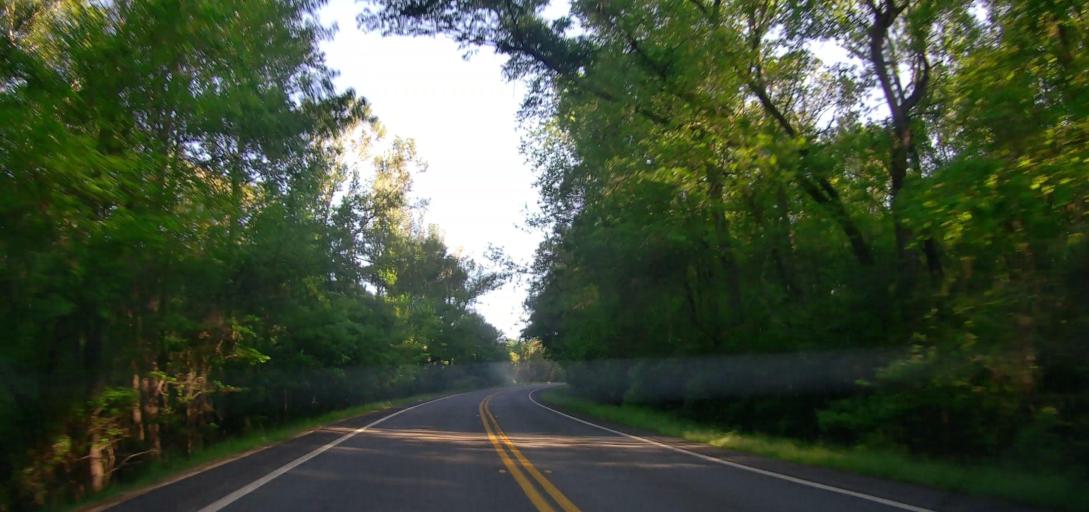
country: US
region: Georgia
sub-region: Macon County
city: Oglethorpe
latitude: 32.3008
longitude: -84.1560
